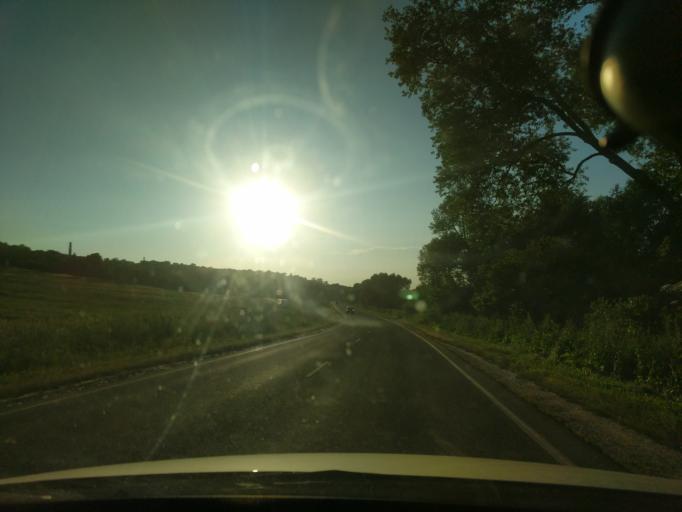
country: RU
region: Moskovskaya
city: Danki
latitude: 54.8472
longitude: 37.5012
